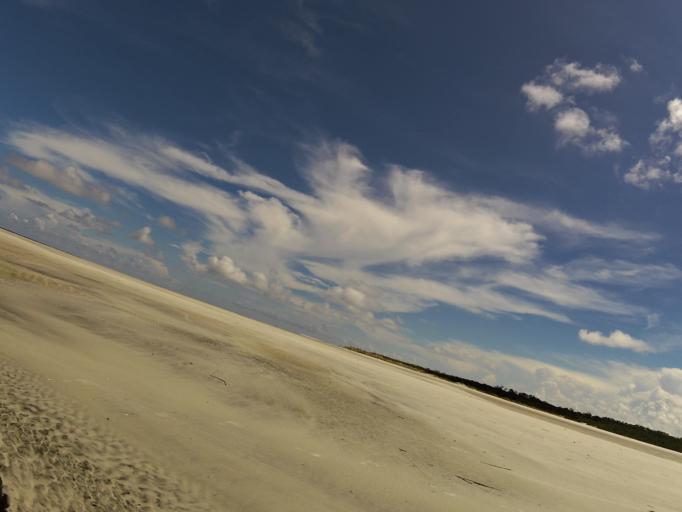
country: US
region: Florida
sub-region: Duval County
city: Atlantic Beach
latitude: 30.4885
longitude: -81.4177
